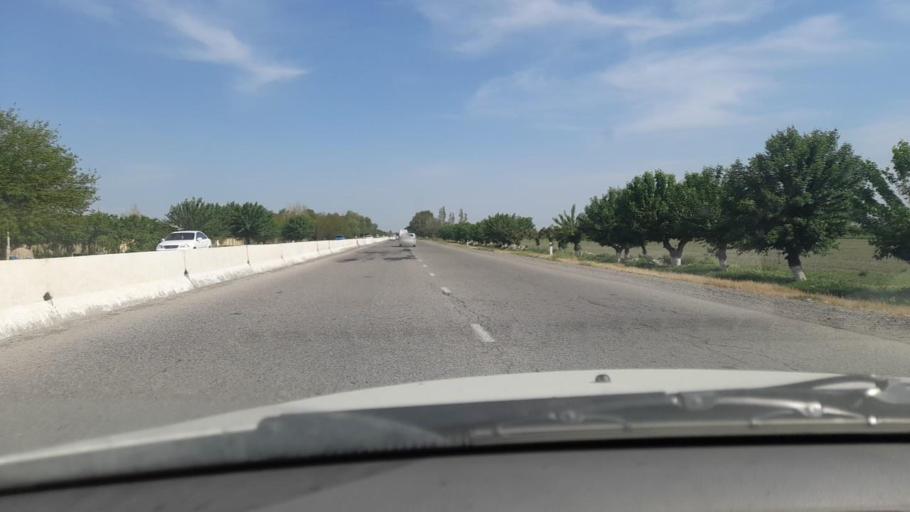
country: UZ
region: Samarqand
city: Chelak
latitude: 39.8483
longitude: 66.8055
